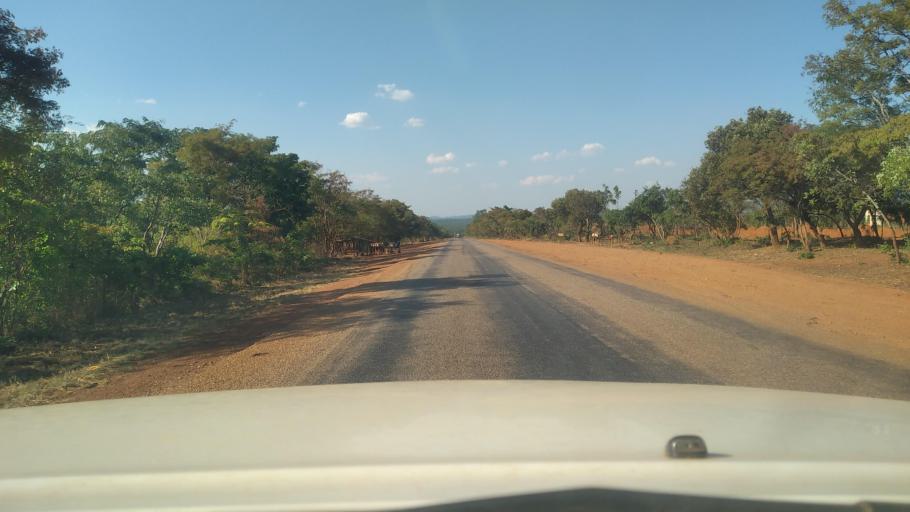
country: ZM
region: Northern
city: Mpika
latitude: -11.7613
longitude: 31.4631
